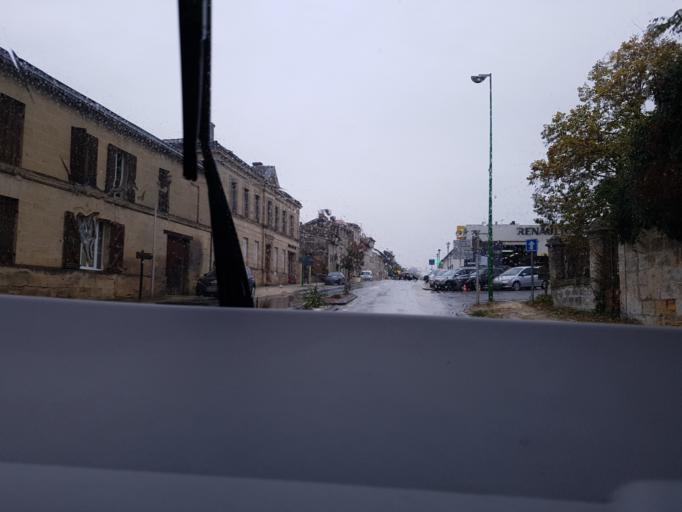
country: FR
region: Aquitaine
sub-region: Departement de la Gironde
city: Cubzac-les-Ponts
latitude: 44.9692
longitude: -0.4546
